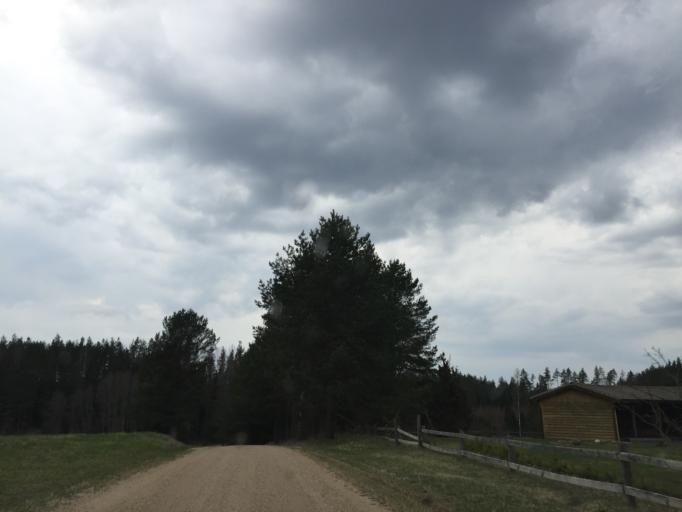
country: EE
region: Vorumaa
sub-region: Antsla vald
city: Vana-Antsla
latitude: 57.9482
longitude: 26.7138
